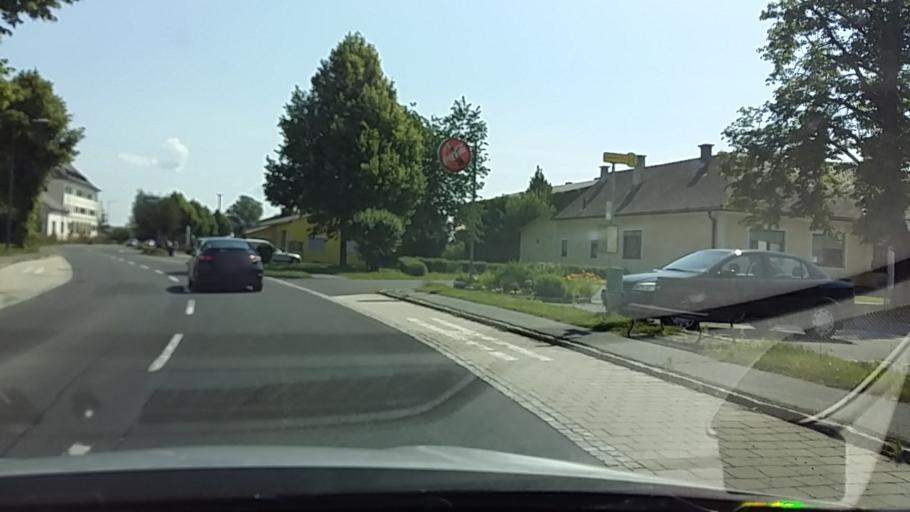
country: AT
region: Burgenland
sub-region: Politischer Bezirk Jennersdorf
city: Mogersdorf
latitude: 46.9478
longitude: 16.2341
